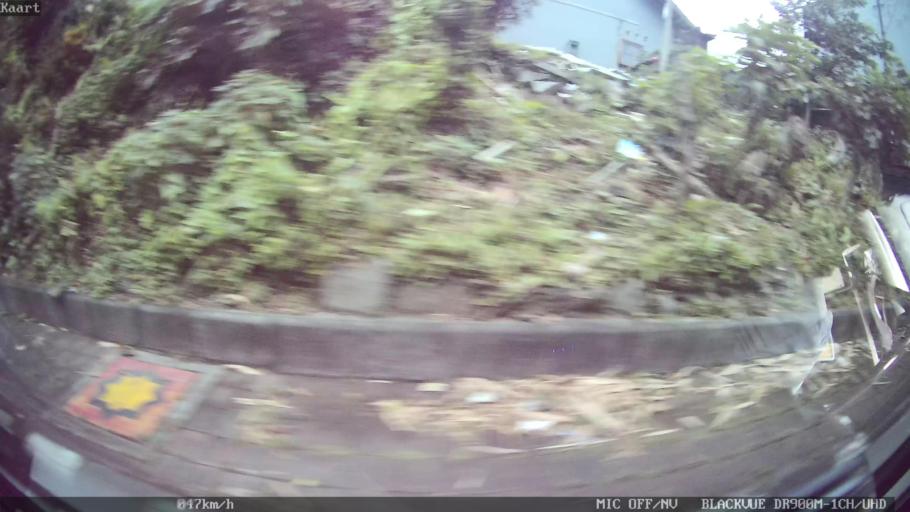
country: ID
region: Bali
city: Banjar Pekenjelodan
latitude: -8.5650
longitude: 115.1754
